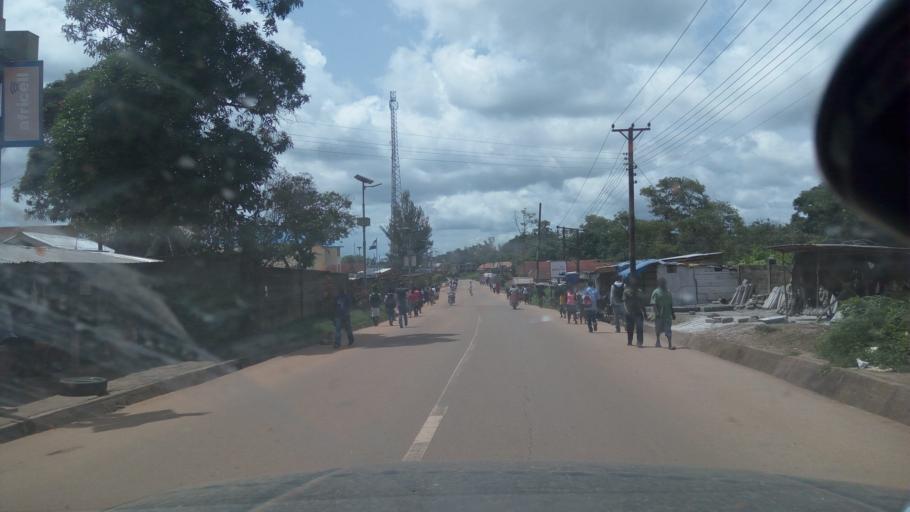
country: SL
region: Eastern Province
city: Kenema
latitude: 7.8756
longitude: -11.1842
